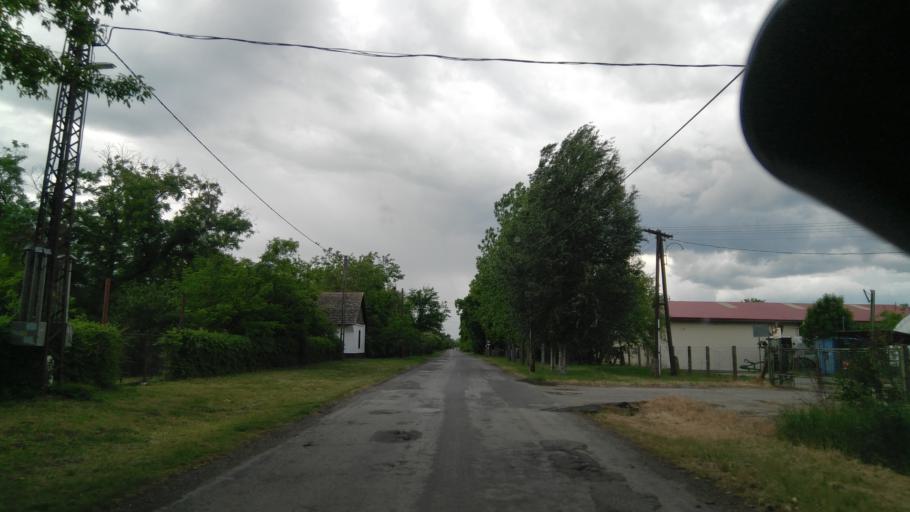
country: HU
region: Bekes
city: Gadoros
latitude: 46.6724
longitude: 20.5756
